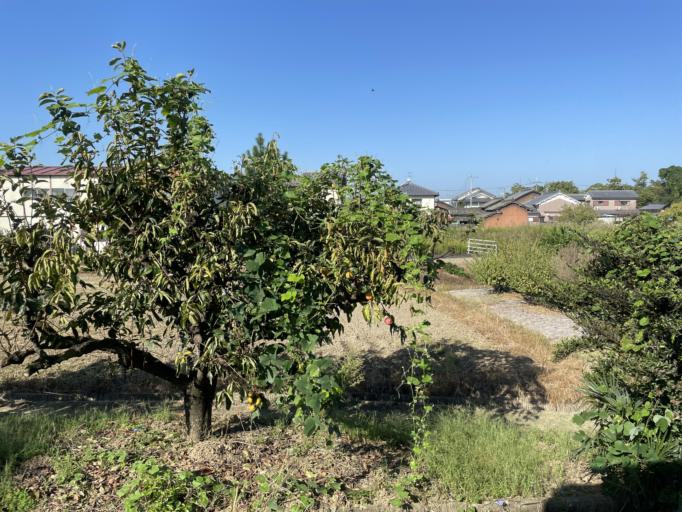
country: JP
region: Nara
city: Tawaramoto
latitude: 34.5428
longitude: 135.7940
